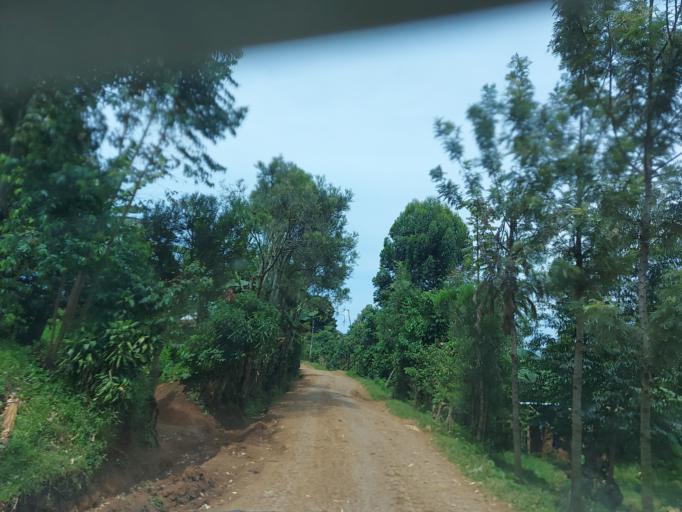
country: CD
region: South Kivu
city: Bukavu
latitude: -2.2371
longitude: 28.8456
